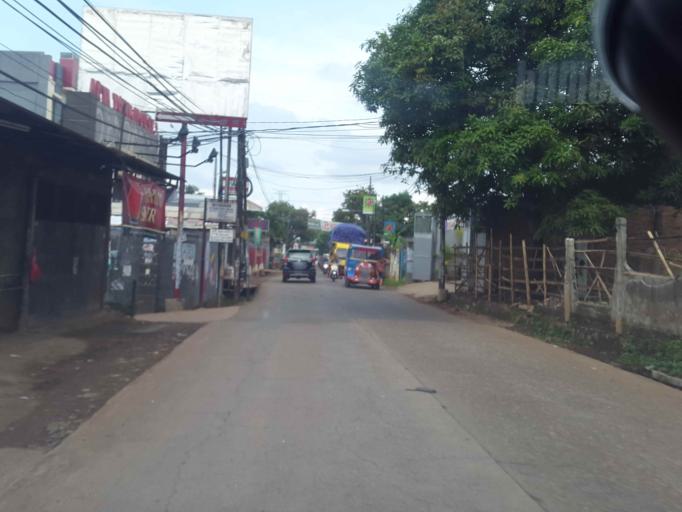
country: ID
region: West Java
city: Cileungsir
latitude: -6.3617
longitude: 106.9206
